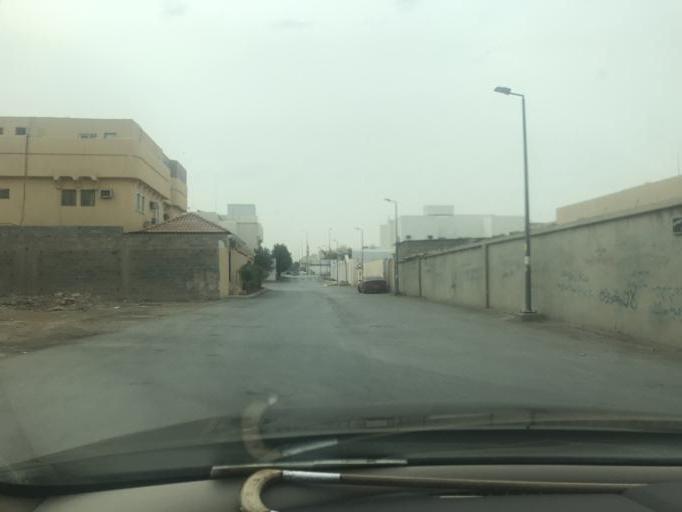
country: SA
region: Ar Riyad
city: Riyadh
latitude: 24.7497
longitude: 46.7714
